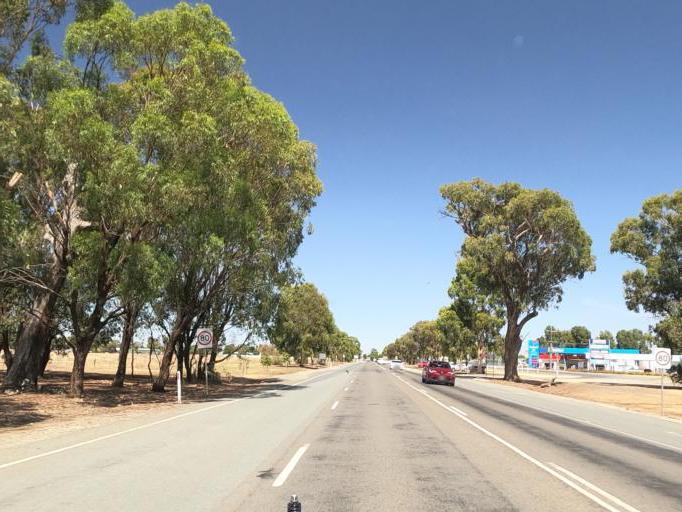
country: AU
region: Victoria
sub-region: Moira
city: Yarrawonga
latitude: -36.0128
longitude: 146.0204
